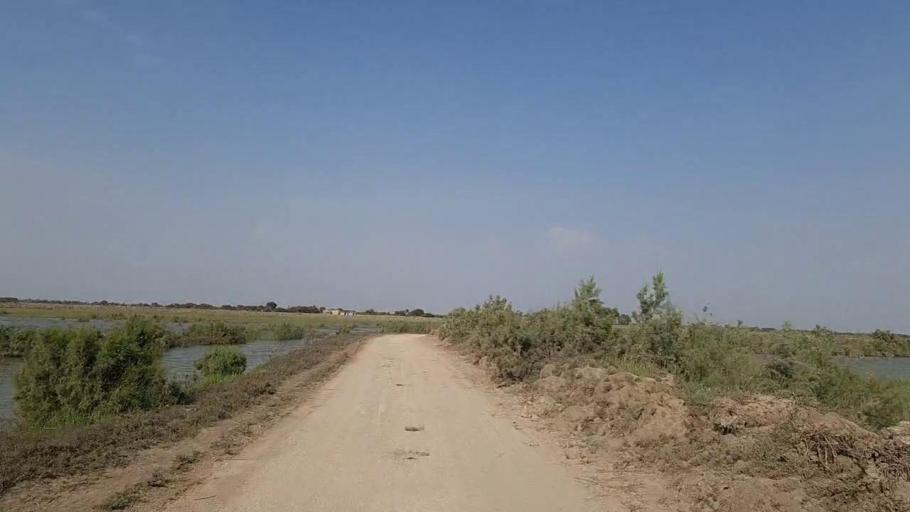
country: PK
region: Sindh
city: Daro Mehar
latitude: 24.7639
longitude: 68.1685
